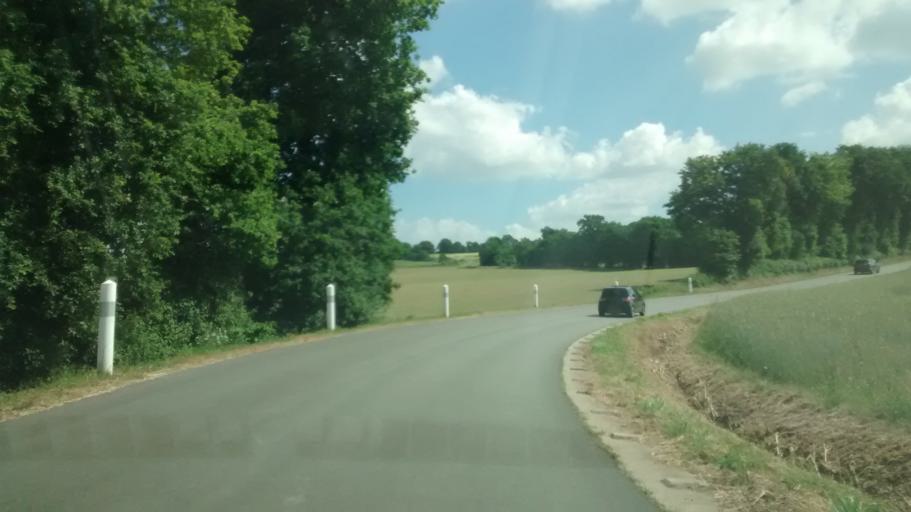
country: FR
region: Brittany
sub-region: Departement du Morbihan
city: Caro
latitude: 47.8465
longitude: -2.3411
